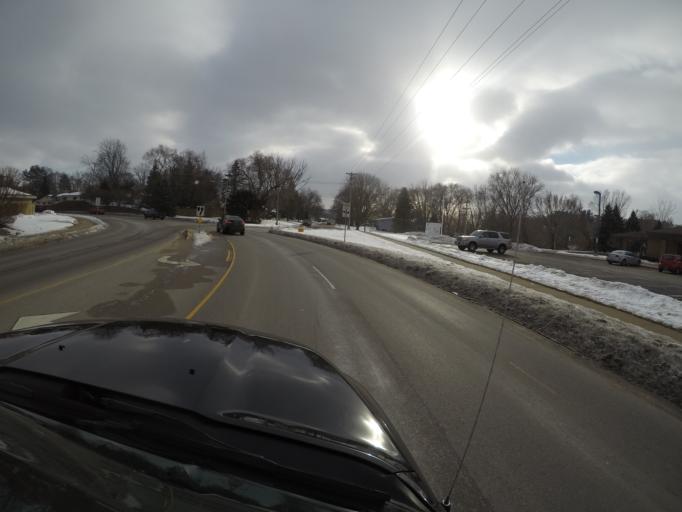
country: US
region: Wisconsin
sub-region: La Crosse County
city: Onalaska
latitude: 43.8810
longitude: -91.2083
